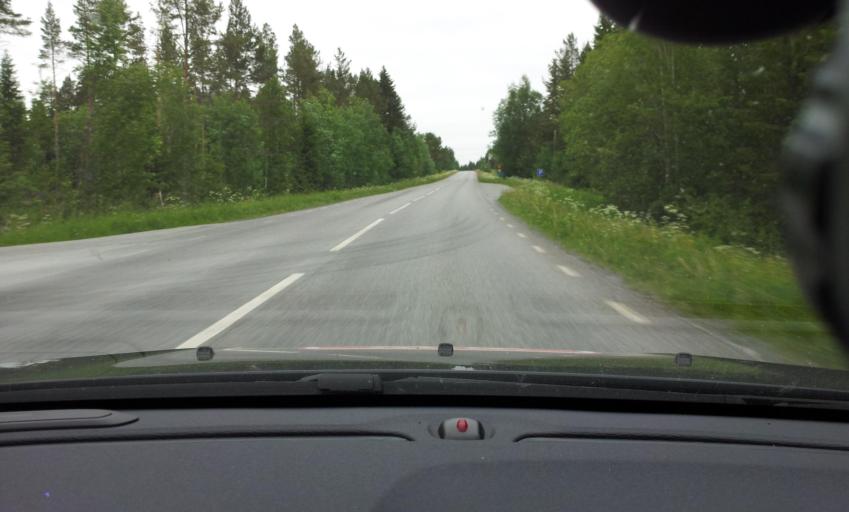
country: SE
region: Jaemtland
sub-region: Krokoms Kommun
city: Valla
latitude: 63.2081
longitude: 14.0252
